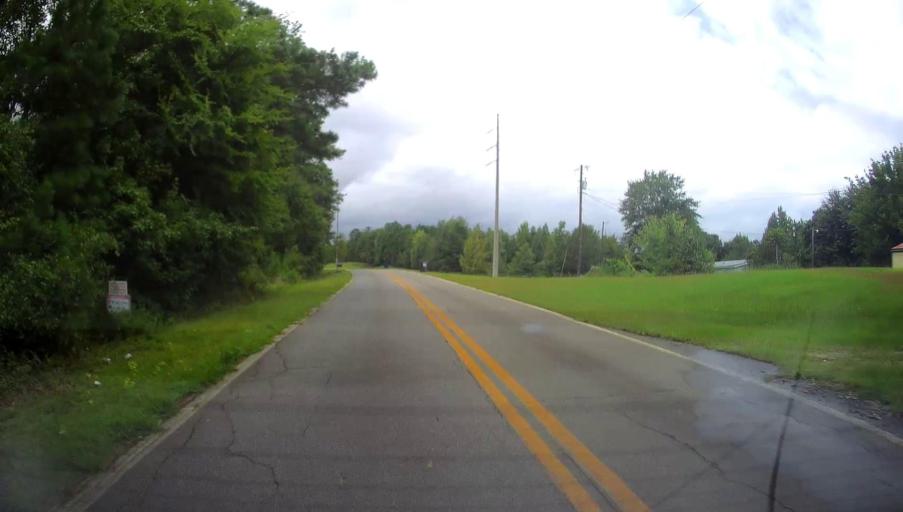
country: US
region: Georgia
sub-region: Bibb County
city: Macon
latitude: 32.7912
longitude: -83.5184
